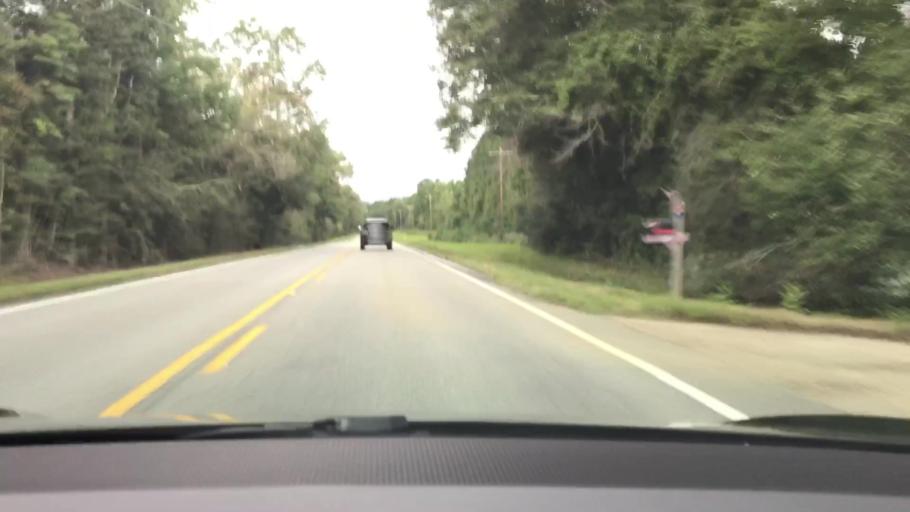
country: US
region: Alabama
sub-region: Coffee County
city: Elba
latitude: 31.4712
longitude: -86.0621
